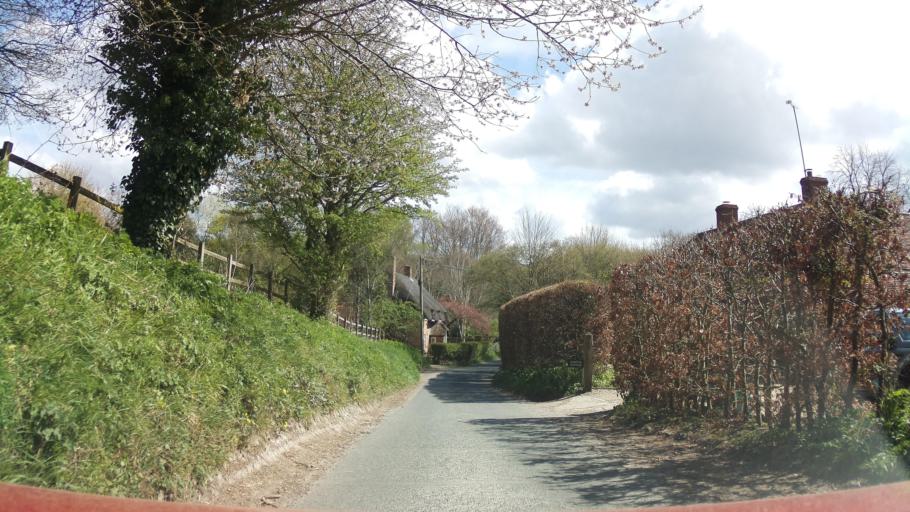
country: GB
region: England
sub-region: West Berkshire
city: Kintbury
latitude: 51.3477
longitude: -1.4699
